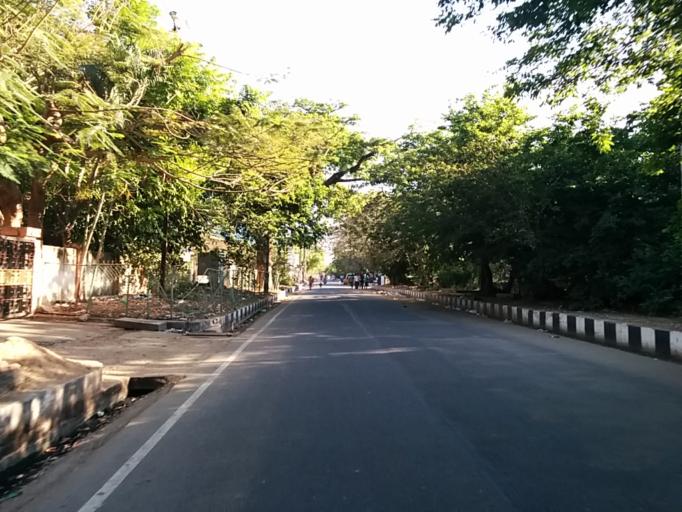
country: IN
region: Pondicherry
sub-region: Puducherry
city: Puducherry
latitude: 11.9225
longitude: 79.8306
